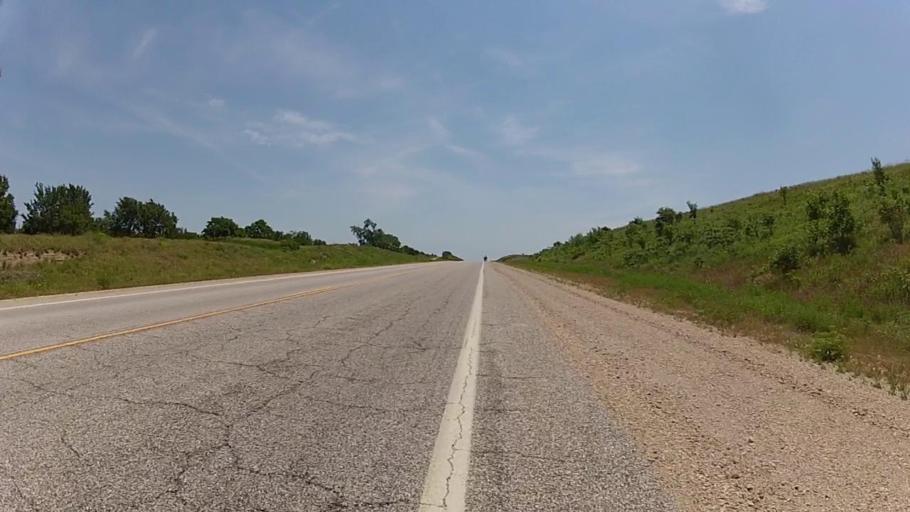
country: US
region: Kansas
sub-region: Chautauqua County
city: Sedan
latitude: 37.1131
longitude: -96.4441
